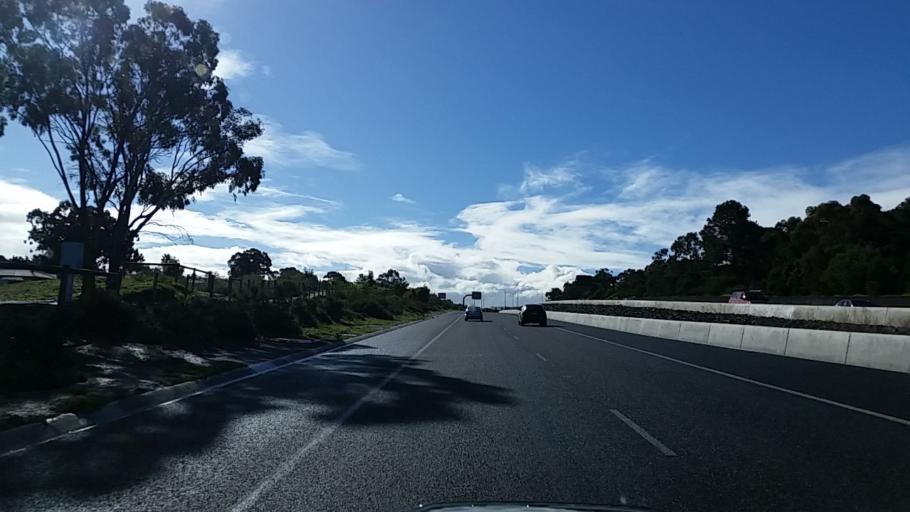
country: AU
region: South Australia
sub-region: Onkaparinga
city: Noarlunga Downs
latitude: -35.1471
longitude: 138.5054
